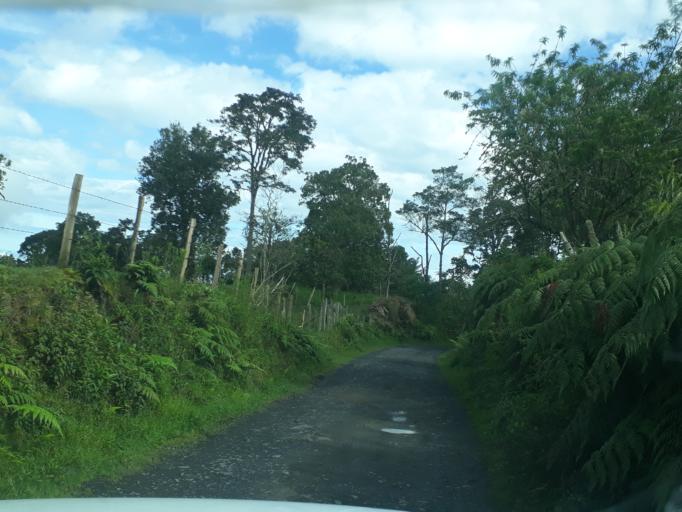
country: CO
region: Cundinamarca
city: Carmen de Carupa
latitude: 5.3380
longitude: -74.0554
